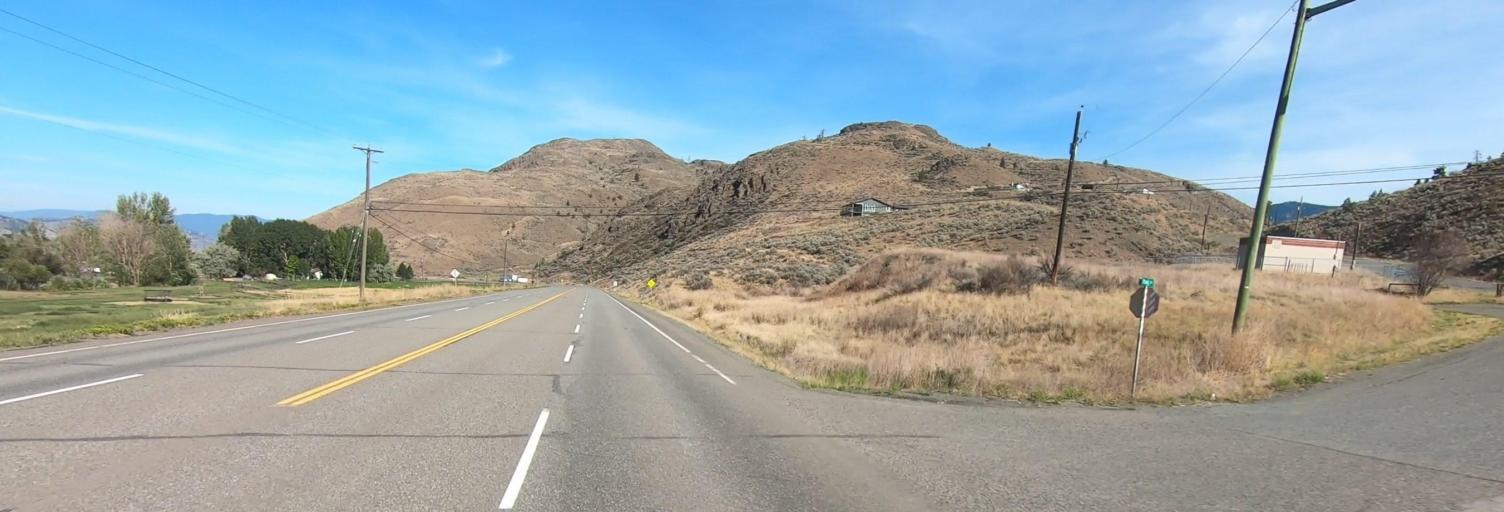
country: CA
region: British Columbia
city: Kamloops
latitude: 50.6998
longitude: -120.5917
